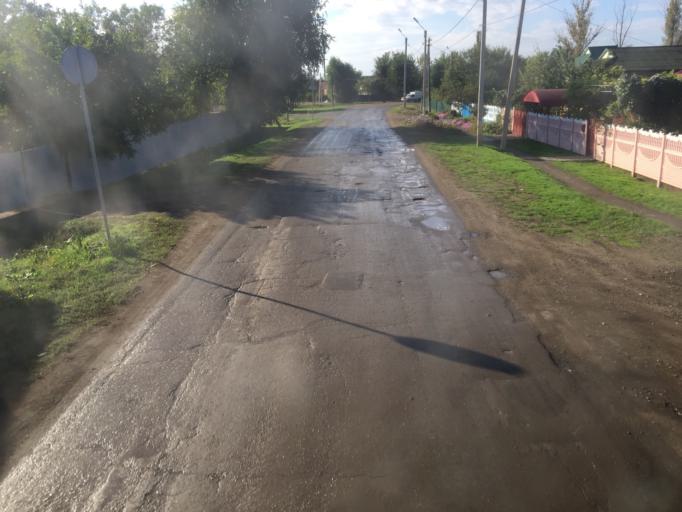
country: RU
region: Rostov
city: Peschanokopskoye
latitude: 46.1904
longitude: 41.0824
